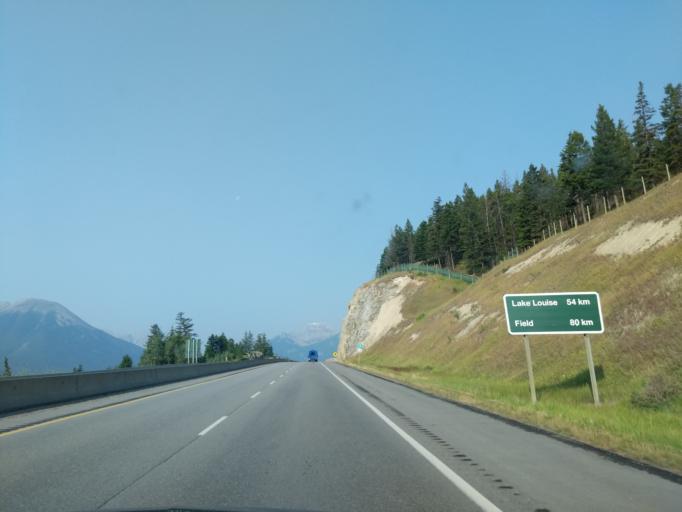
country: CA
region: Alberta
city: Banff
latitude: 51.1857
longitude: -115.5913
